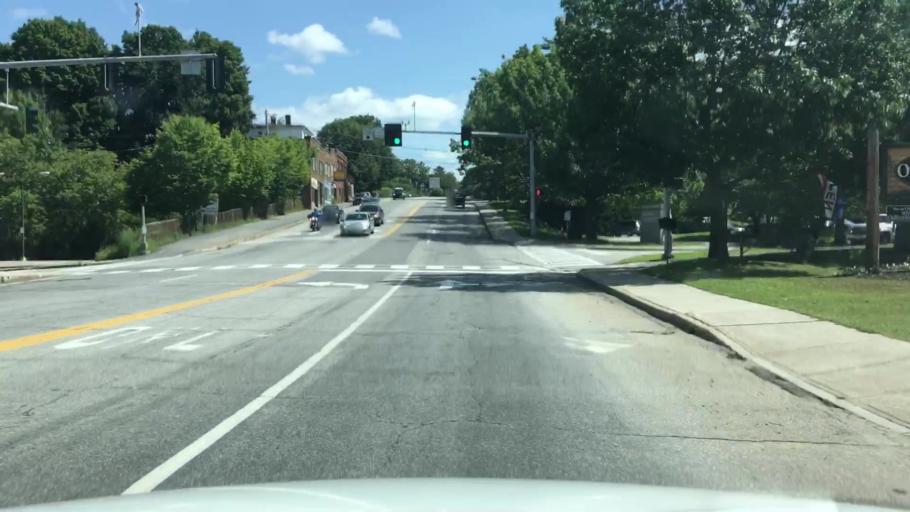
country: US
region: Maine
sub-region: Kennebec County
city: Augusta
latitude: 44.3166
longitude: -69.7710
